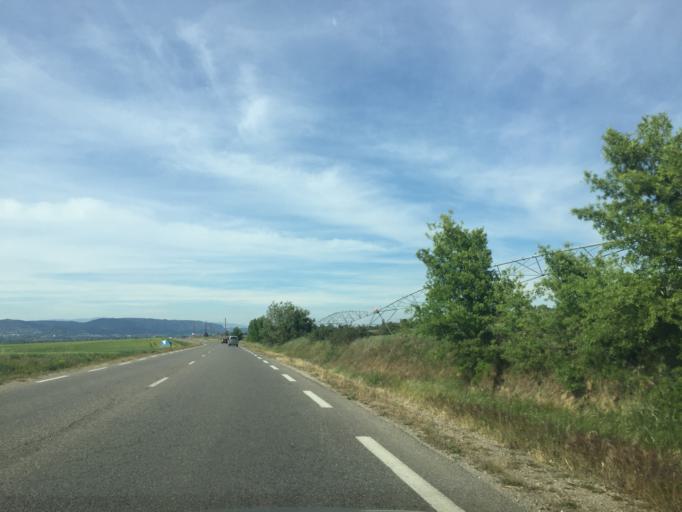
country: FR
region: Provence-Alpes-Cote d'Azur
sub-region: Departement du Var
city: Vinon-sur-Verdon
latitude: 43.7455
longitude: 5.8028
